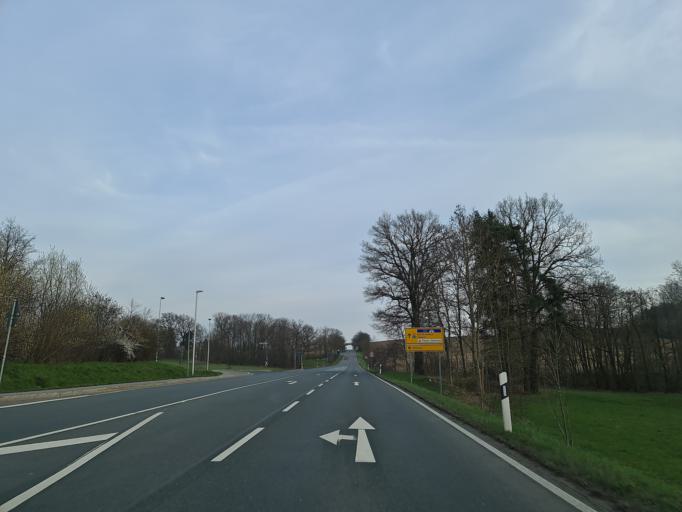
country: DE
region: Saxony
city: Plauen
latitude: 50.4660
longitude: 12.1512
